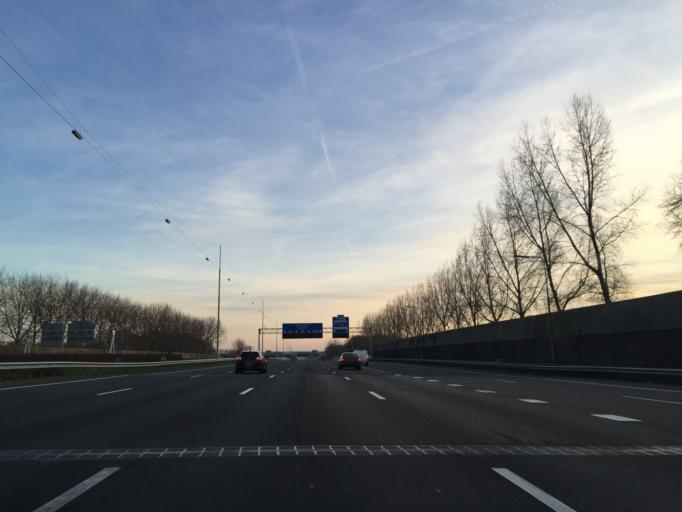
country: NL
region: South Holland
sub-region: Gemeente Ridderkerk
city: Ridderkerk
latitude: 51.8516
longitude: 4.6023
